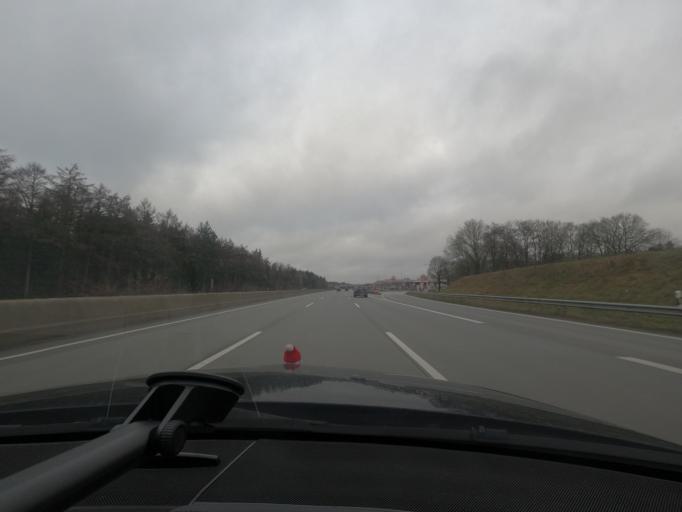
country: DE
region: Schleswig-Holstein
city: Padenstedt
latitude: 54.0104
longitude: 9.9321
